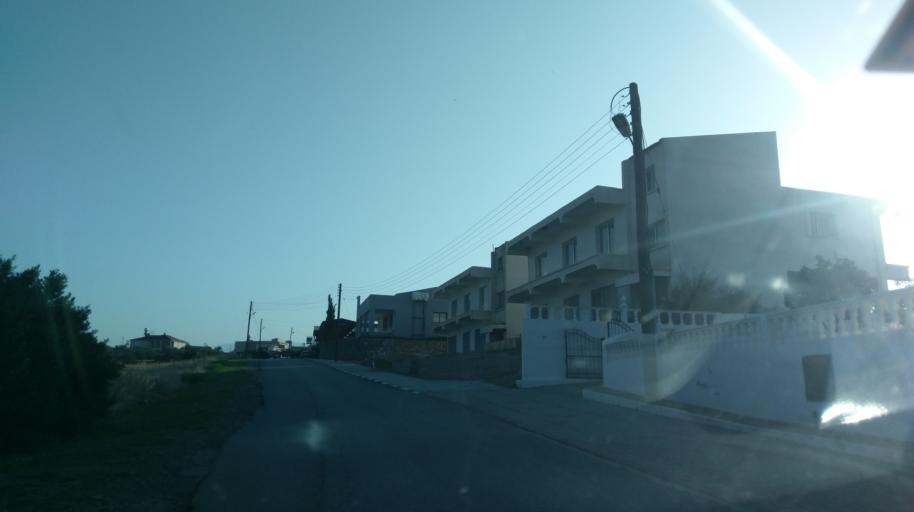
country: CY
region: Lefkosia
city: Lefka
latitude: 35.1394
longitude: 32.9135
